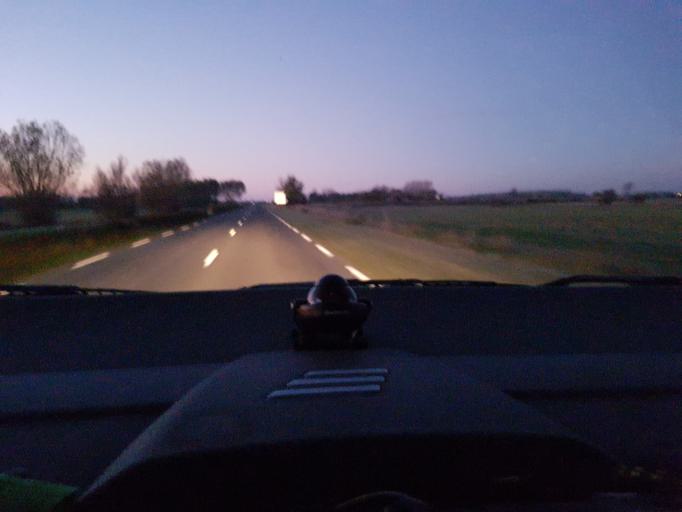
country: FR
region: Picardie
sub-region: Departement de la Somme
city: Pende
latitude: 50.1964
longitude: 1.5569
